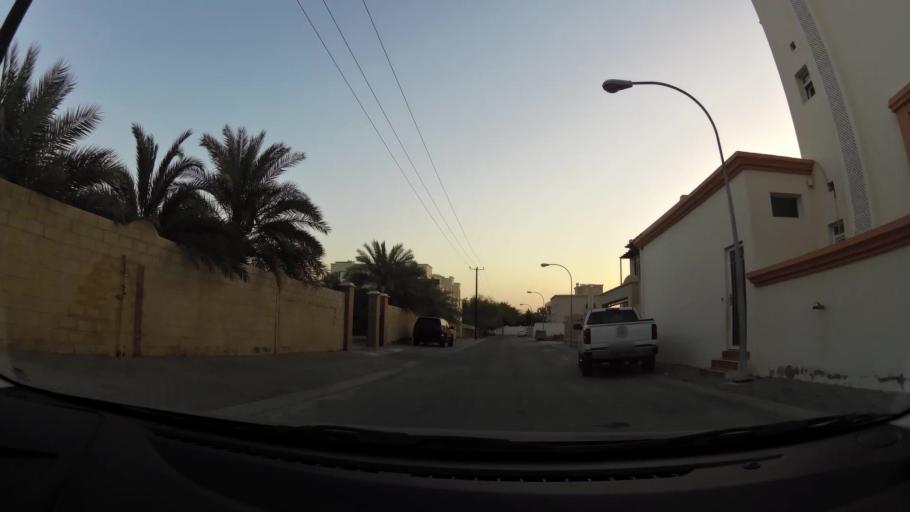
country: OM
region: Muhafazat Masqat
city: As Sib al Jadidah
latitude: 23.6456
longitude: 58.2058
